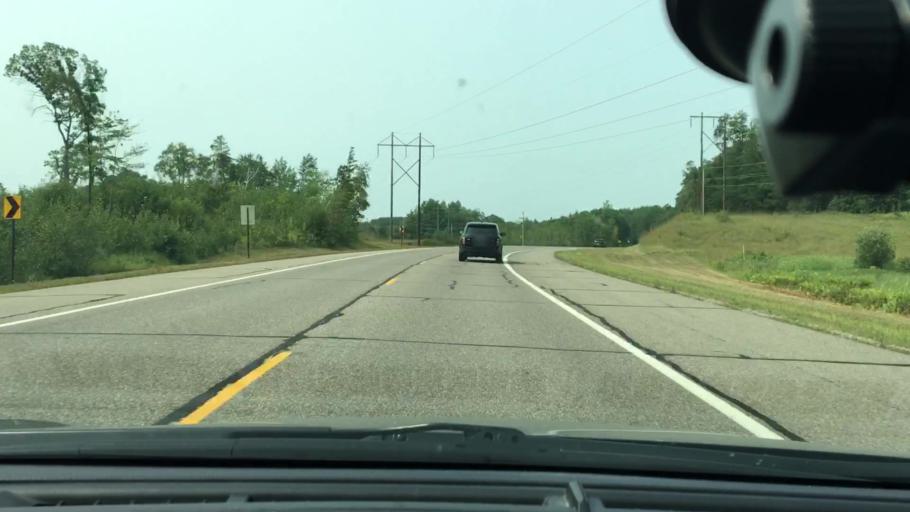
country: US
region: Minnesota
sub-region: Cass County
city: East Gull Lake
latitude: 46.3833
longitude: -94.3231
